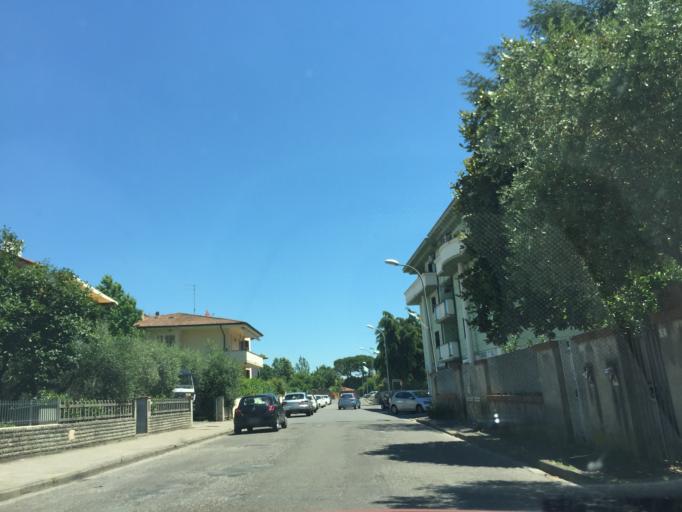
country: IT
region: Tuscany
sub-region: Province of Pisa
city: San Miniato
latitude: 43.6859
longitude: 10.7966
